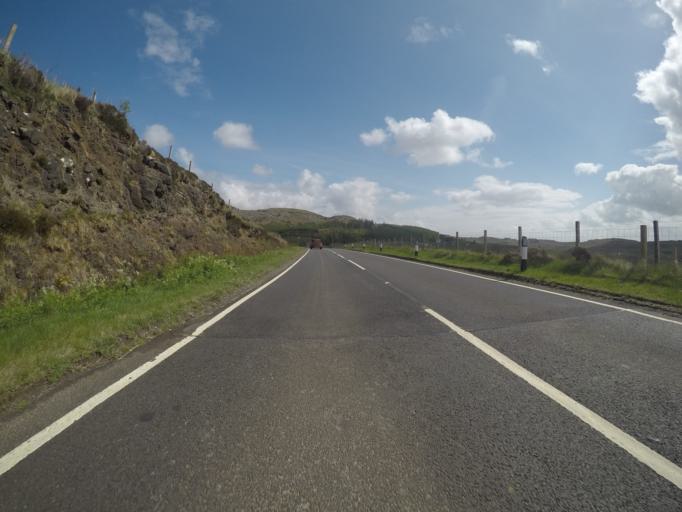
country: GB
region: Scotland
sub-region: Highland
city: Portree
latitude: 57.5324
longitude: -6.3547
